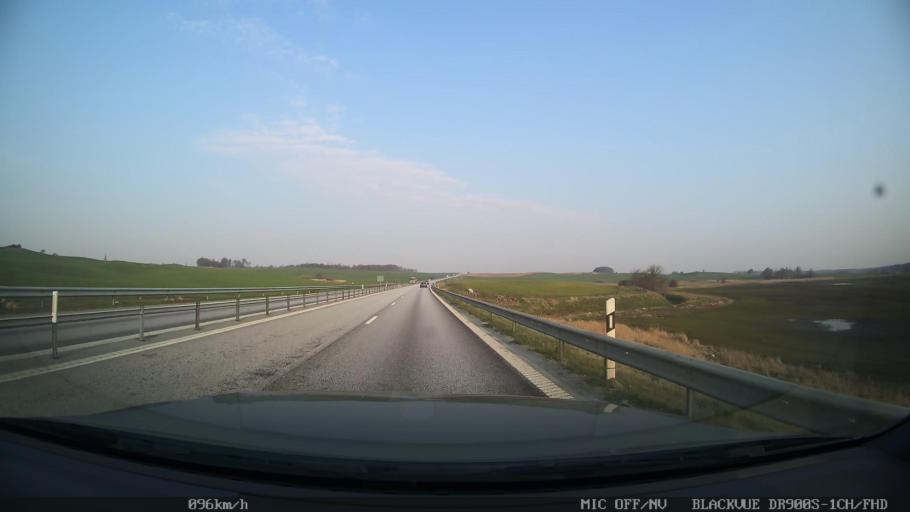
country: SE
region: Skane
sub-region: Ystads Kommun
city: Ystad
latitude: 55.4589
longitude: 13.7312
